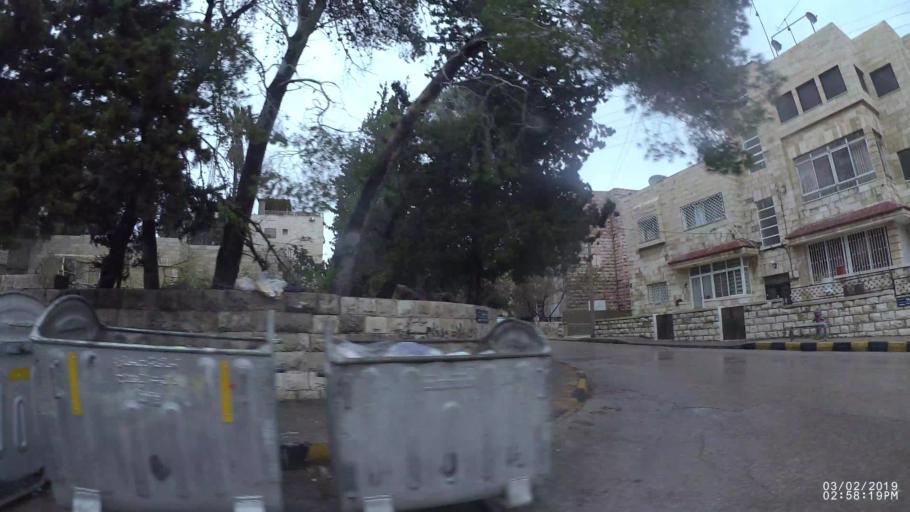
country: JO
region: Amman
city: Amman
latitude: 31.9618
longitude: 35.9173
